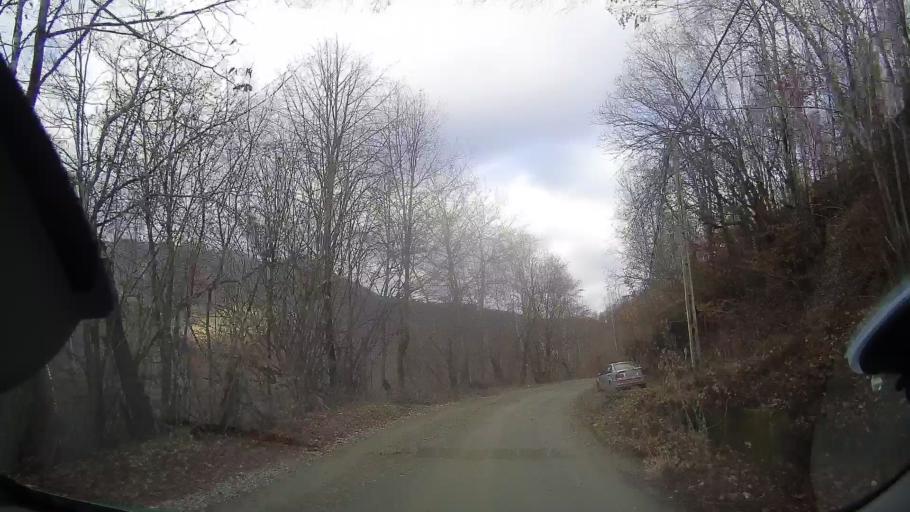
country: RO
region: Cluj
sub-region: Comuna Valea Ierii
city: Valea Ierii
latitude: 46.6829
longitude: 23.3087
